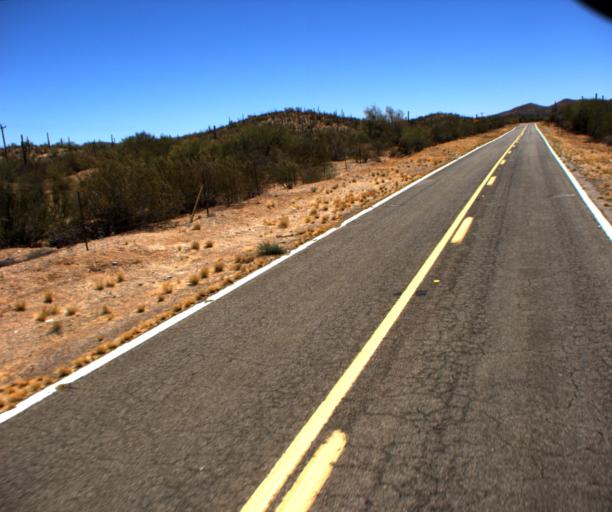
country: US
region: Arizona
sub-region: Pima County
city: Sells
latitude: 32.1747
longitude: -112.2250
